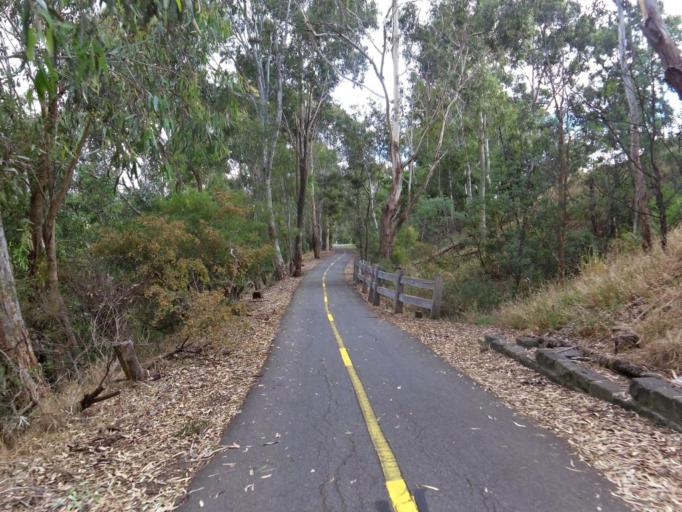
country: AU
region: Victoria
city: Heidelberg West
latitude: -37.7526
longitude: 145.0321
